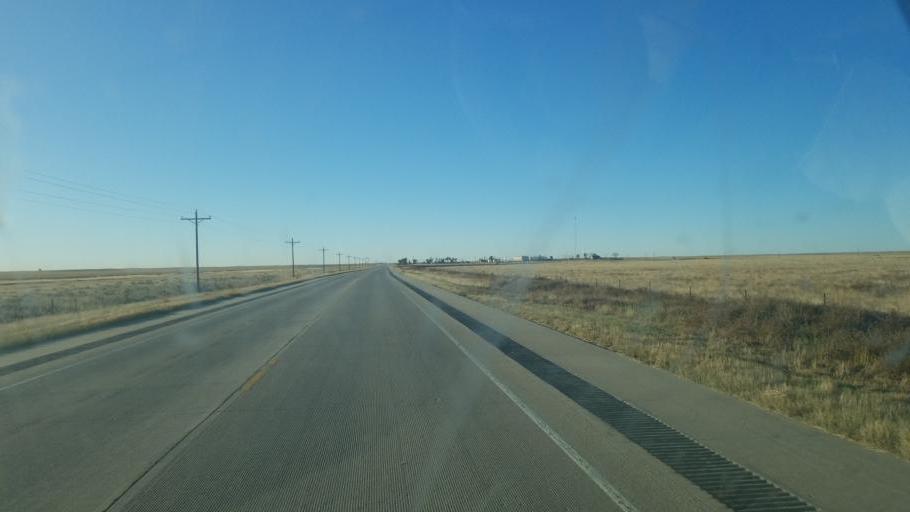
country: US
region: Colorado
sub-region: Kiowa County
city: Eads
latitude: 38.6714
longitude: -102.7861
